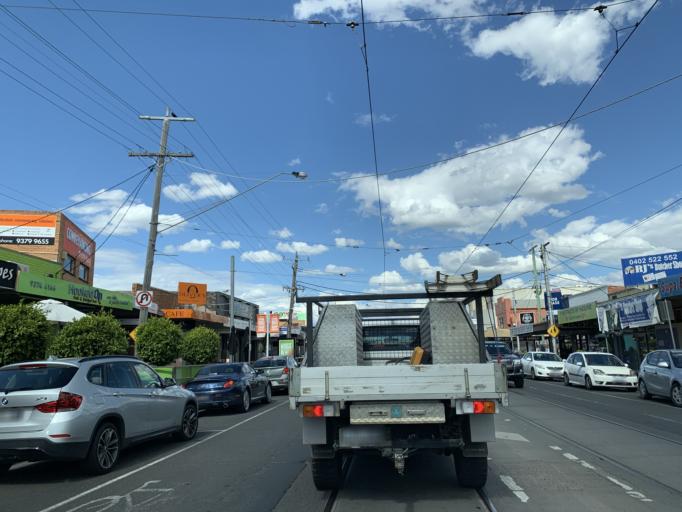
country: AU
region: Victoria
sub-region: Moonee Valley
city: Niddrie
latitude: -37.7362
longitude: 144.8896
